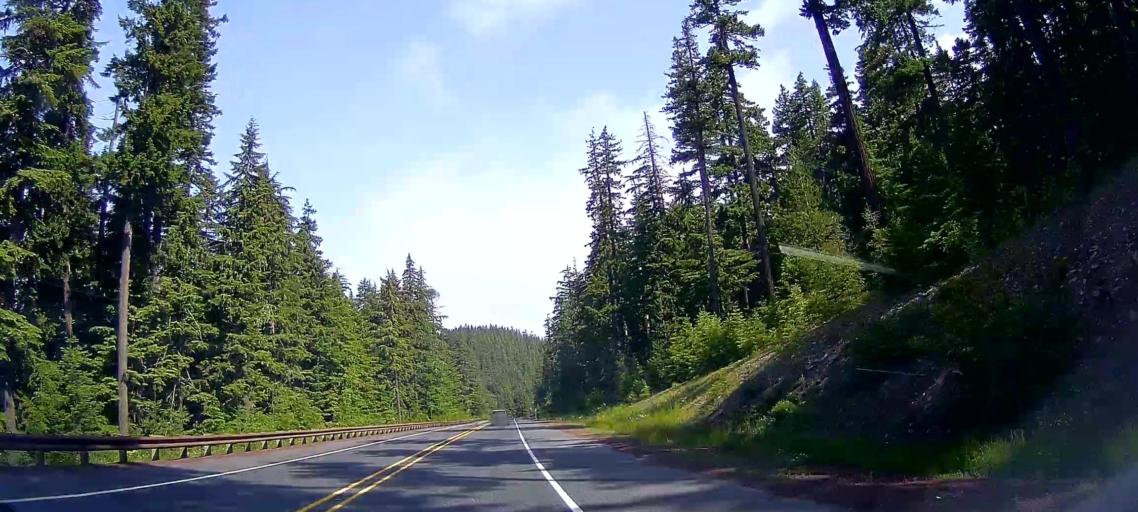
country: US
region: Oregon
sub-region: Clackamas County
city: Mount Hood Village
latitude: 45.2052
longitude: -121.6961
